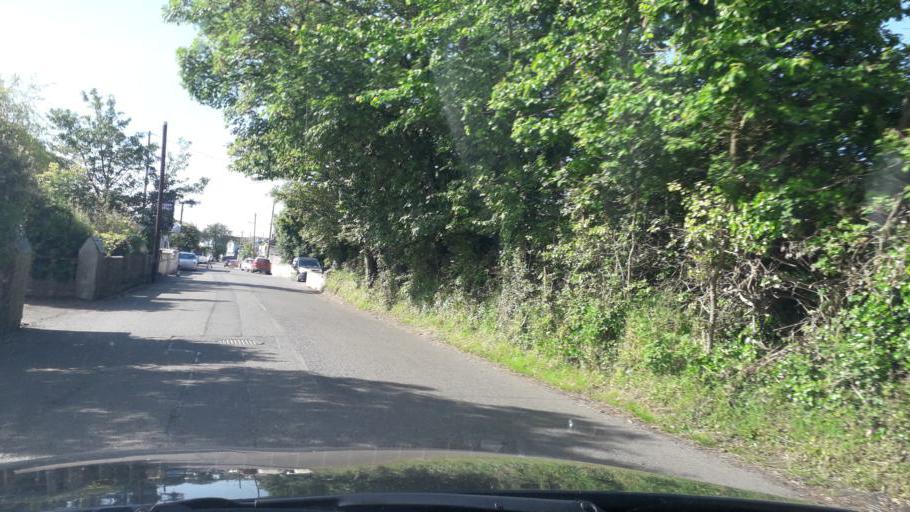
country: IE
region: Leinster
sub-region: Loch Garman
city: Loch Garman
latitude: 52.2329
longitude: -6.5532
